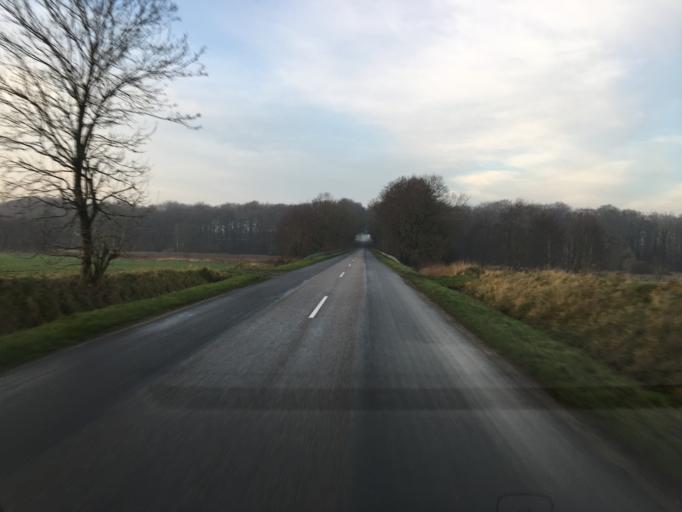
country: DK
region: South Denmark
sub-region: Tonder Kommune
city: Toftlund
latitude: 55.1404
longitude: 9.0550
